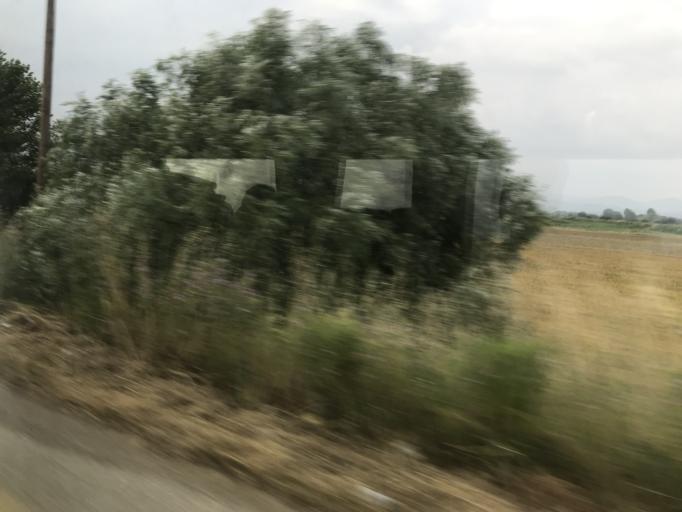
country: GR
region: East Macedonia and Thrace
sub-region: Nomos Rodopis
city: Arisvi
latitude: 41.0538
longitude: 25.6165
